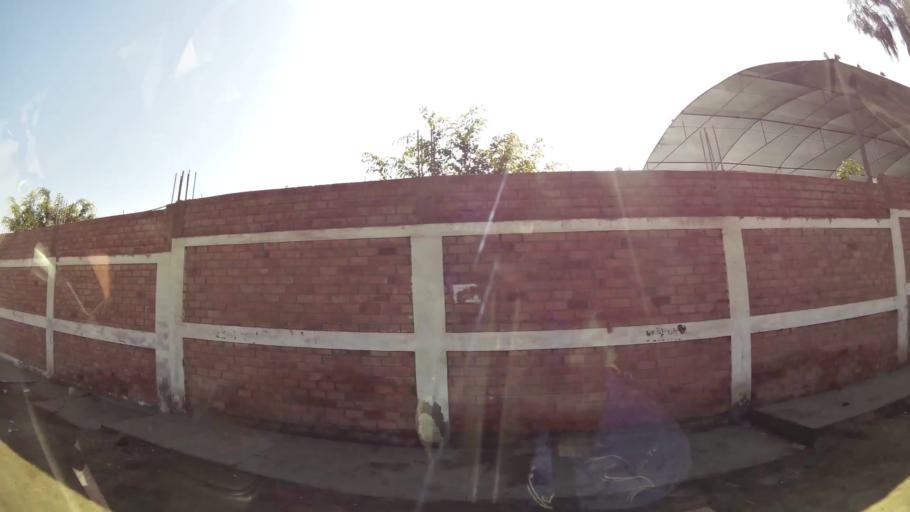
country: PE
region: Ica
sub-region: Provincia de Chincha
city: Chincha Alta
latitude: -13.4144
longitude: -76.1278
